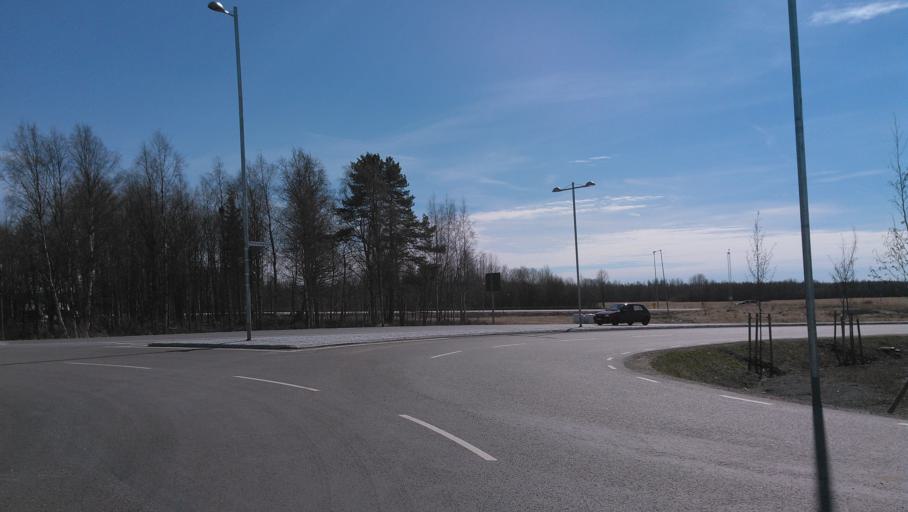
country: SE
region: Vaesterbotten
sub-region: Umea Kommun
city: Umea
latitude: 63.8048
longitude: 20.2567
